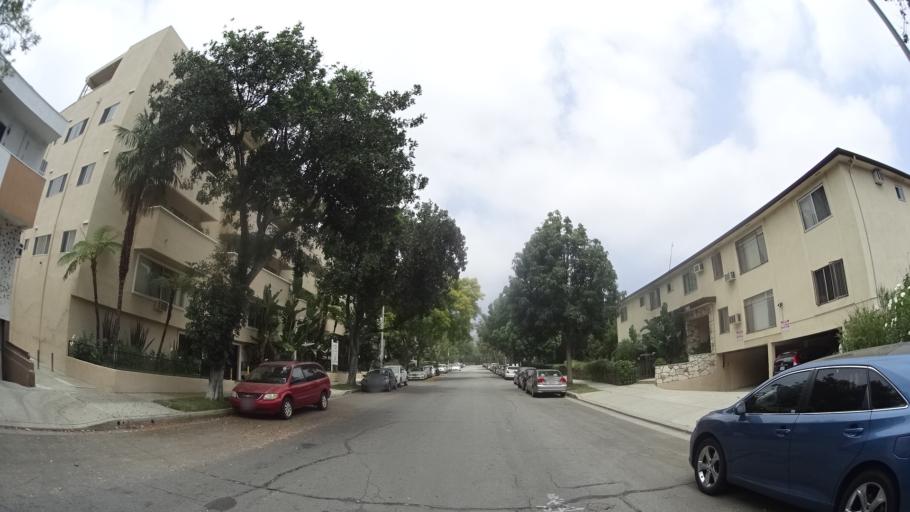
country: US
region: California
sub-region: Los Angeles County
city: West Hollywood
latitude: 34.0922
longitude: -118.3591
